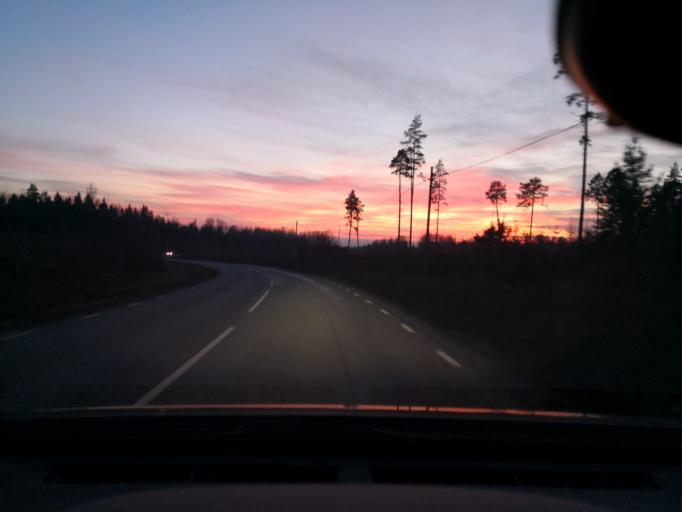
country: SE
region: OErebro
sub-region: Lindesbergs Kommun
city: Frovi
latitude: 59.3619
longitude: 15.4097
